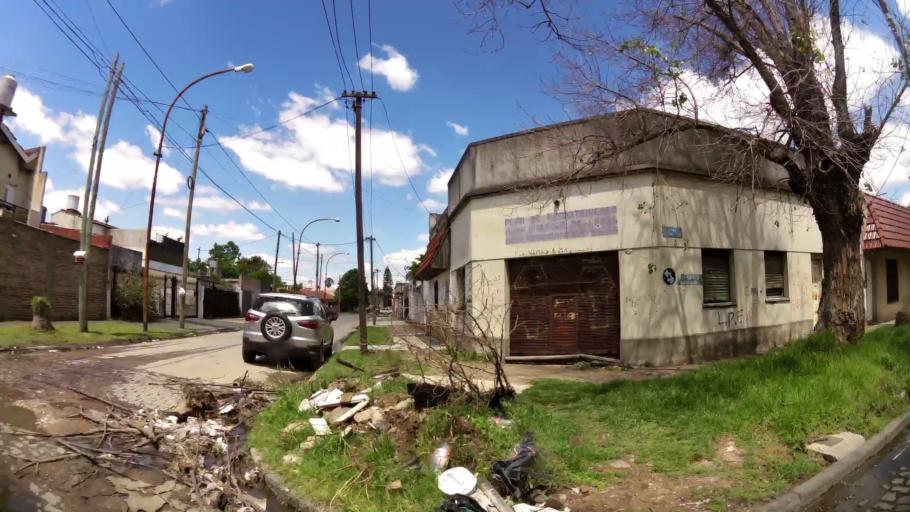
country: AR
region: Buenos Aires
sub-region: Partido de Lomas de Zamora
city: Lomas de Zamora
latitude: -34.7303
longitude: -58.4089
